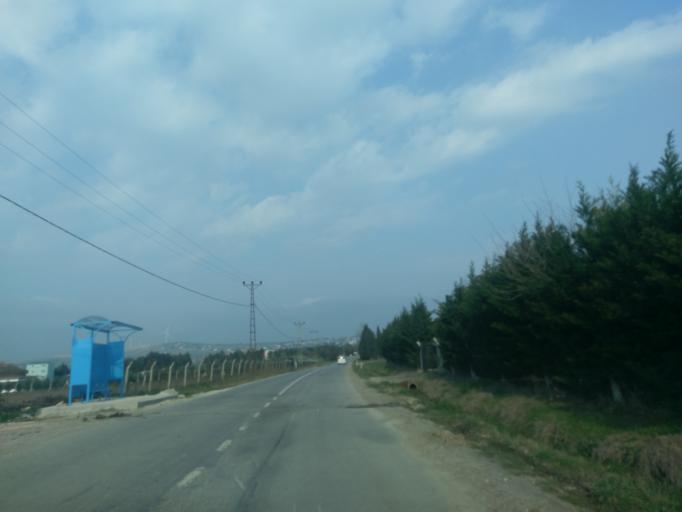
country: TR
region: Istanbul
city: Kavakli
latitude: 41.1115
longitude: 28.2998
